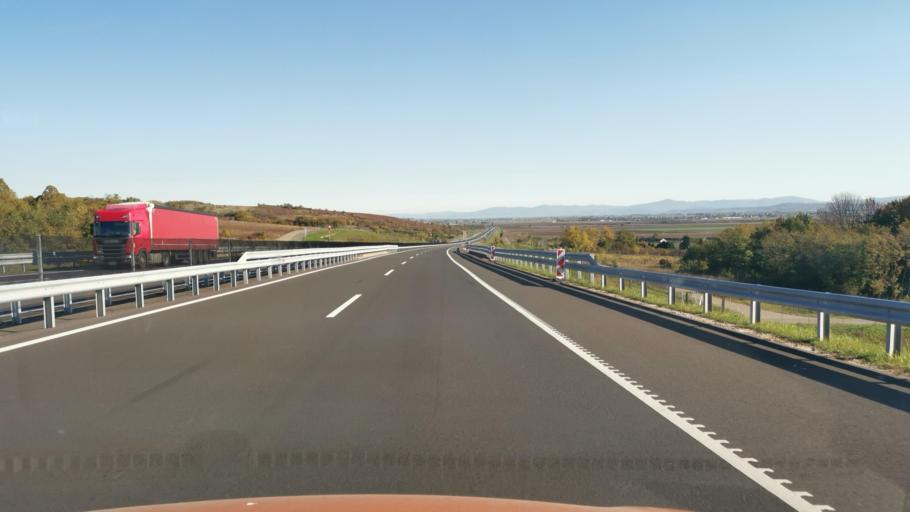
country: HU
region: Borsod-Abauj-Zemplen
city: Aszalo
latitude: 48.2259
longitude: 20.9433
